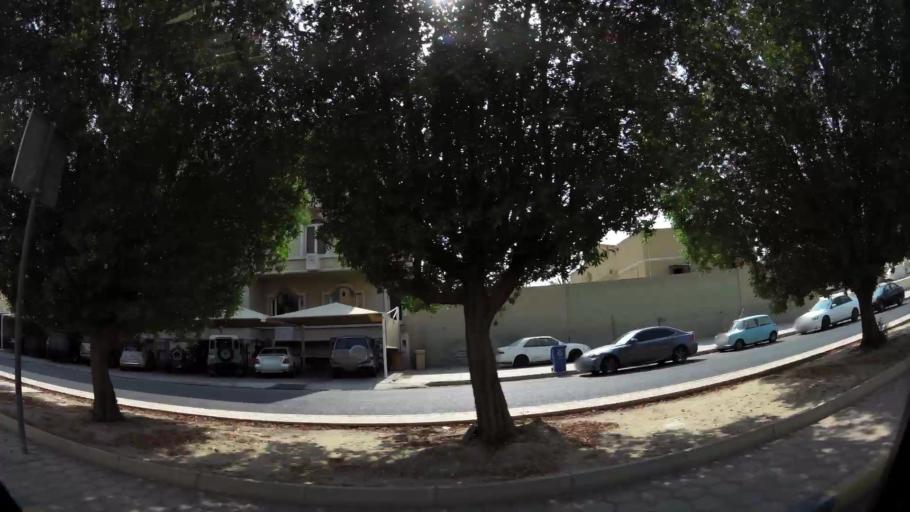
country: KW
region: Muhafazat Hawalli
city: Hawalli
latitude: 29.3477
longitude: 48.0243
